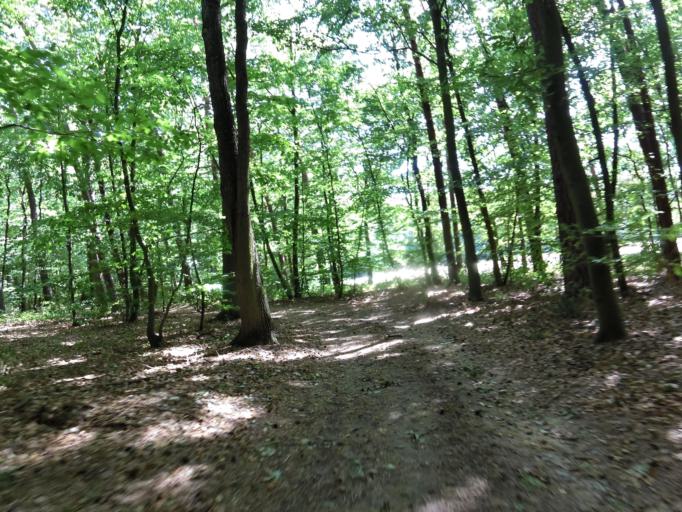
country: DE
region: Bavaria
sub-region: Regierungsbezirk Unterfranken
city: Theilheim
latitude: 49.7448
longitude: 10.0112
